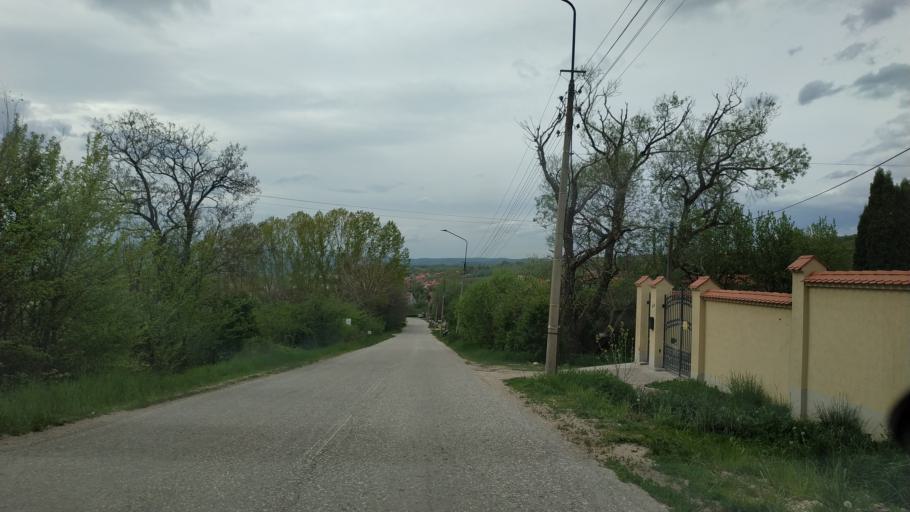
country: RS
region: Central Serbia
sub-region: Zajecarski Okrug
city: Soko Banja
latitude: 43.6437
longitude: 21.8880
